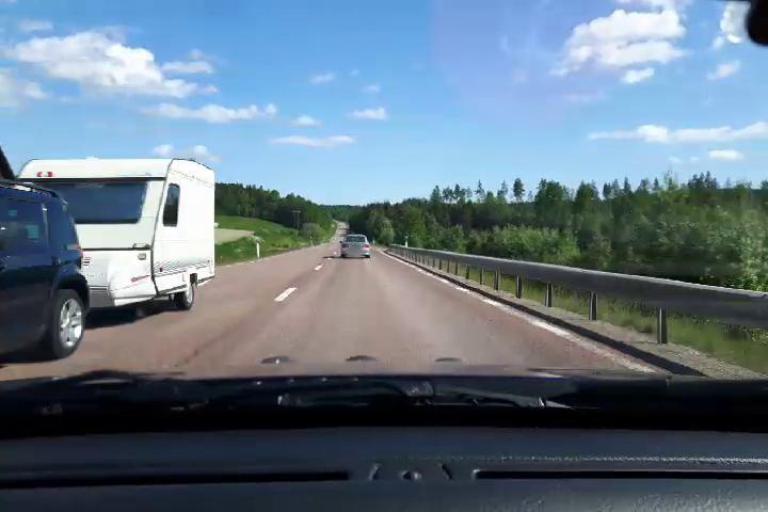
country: SE
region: Gaevleborg
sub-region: Hudiksvalls Kommun
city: Sorforsa
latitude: 61.7482
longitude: 16.8393
